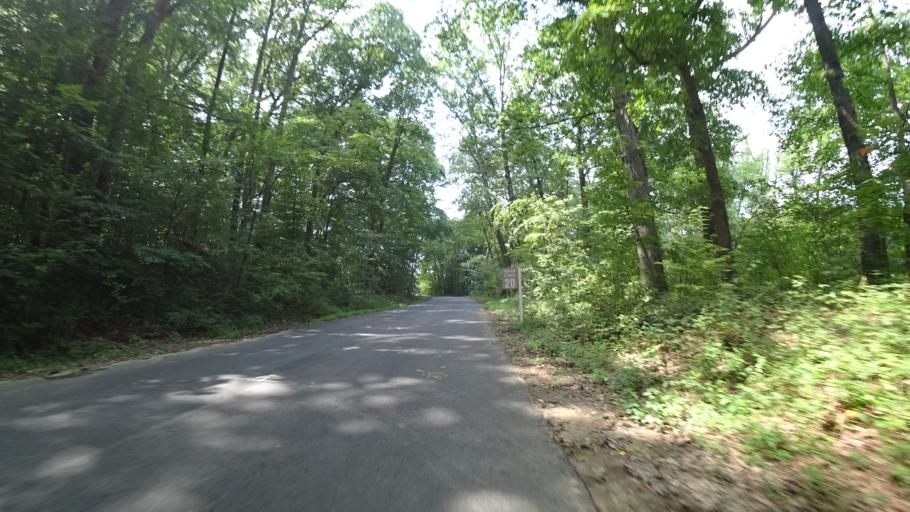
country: US
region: Maryland
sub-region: Prince George's County
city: Colmar Manor
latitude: 38.9124
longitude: -76.9661
